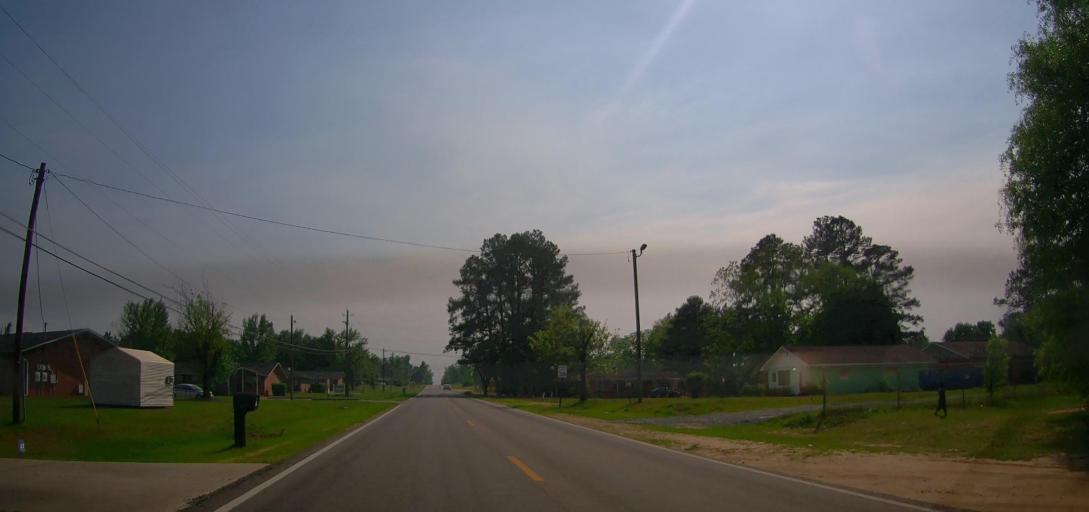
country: US
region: Georgia
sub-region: Laurens County
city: East Dublin
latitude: 32.5578
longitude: -82.8716
